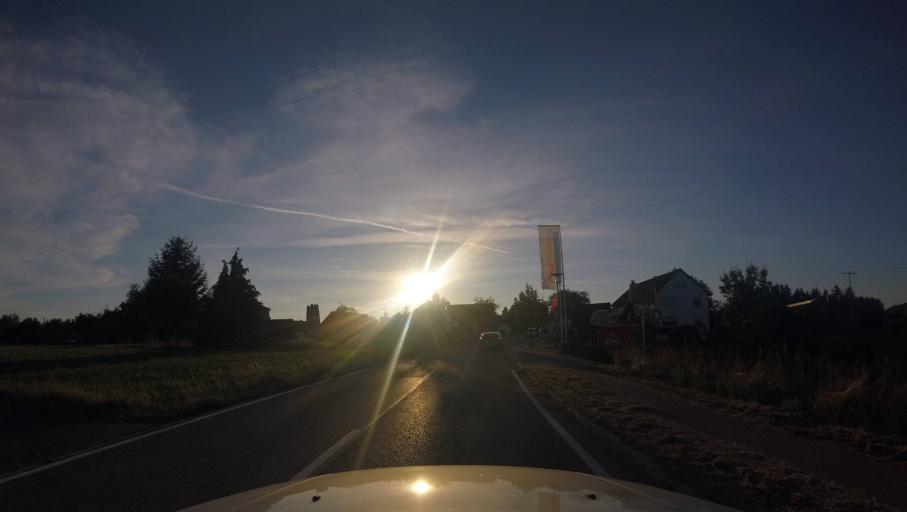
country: DE
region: Baden-Wuerttemberg
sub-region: Regierungsbezirk Stuttgart
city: Althutte
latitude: 48.9207
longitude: 9.6009
